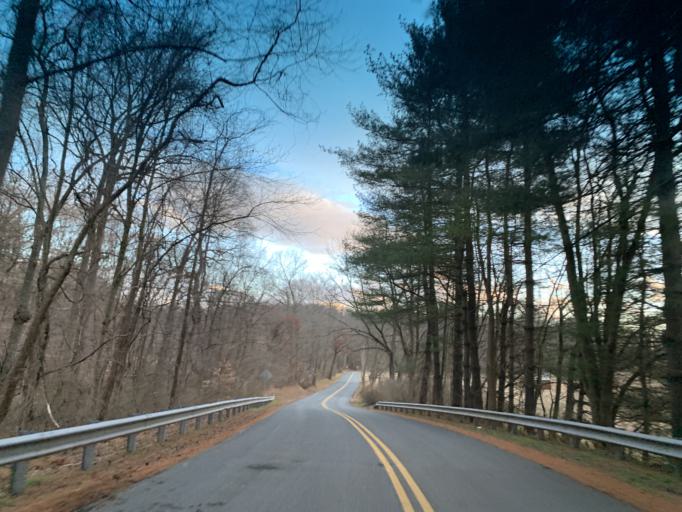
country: US
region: Maryland
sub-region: Harford County
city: Bel Air North
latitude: 39.6252
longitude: -76.3094
